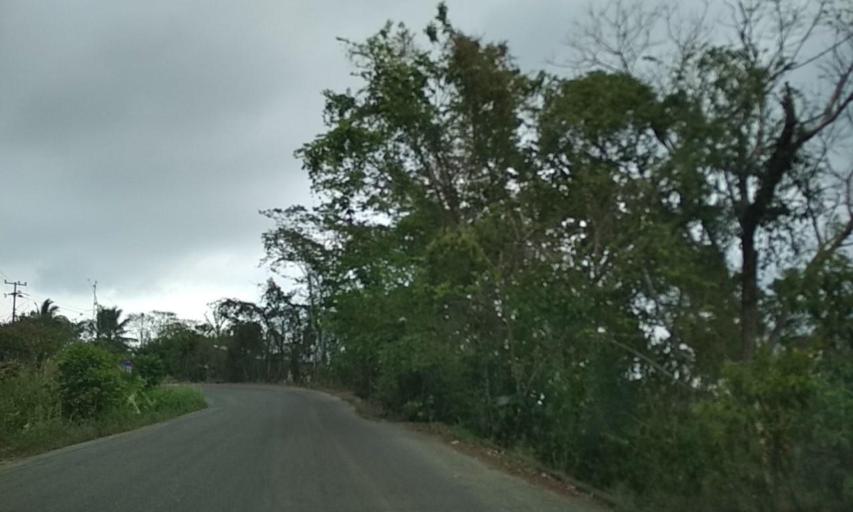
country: MX
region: Tabasco
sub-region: Huimanguillo
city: Francisco Rueda
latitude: 17.5802
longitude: -94.0952
